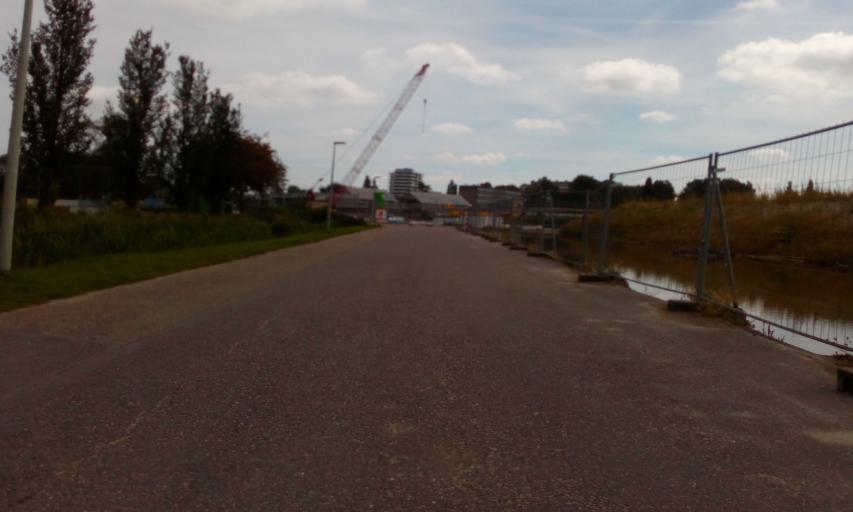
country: NL
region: South Holland
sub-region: Gemeente Schiedam
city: Schiedam
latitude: 51.9205
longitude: 4.3721
